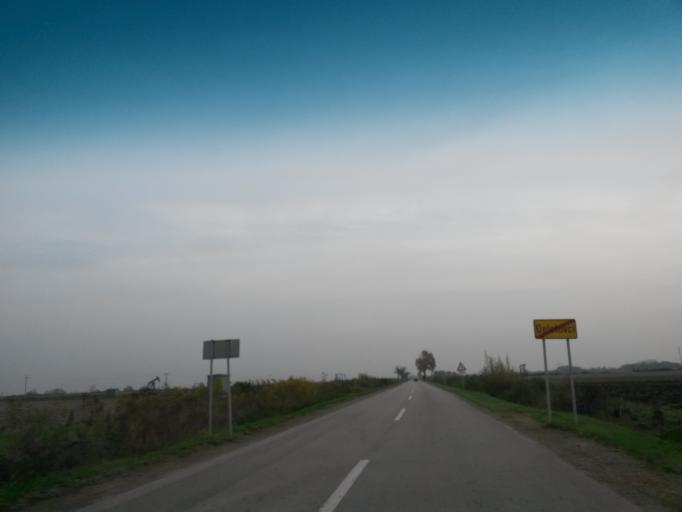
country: HR
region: Vukovarsko-Srijemska
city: Nijemci
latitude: 45.1736
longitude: 19.0148
